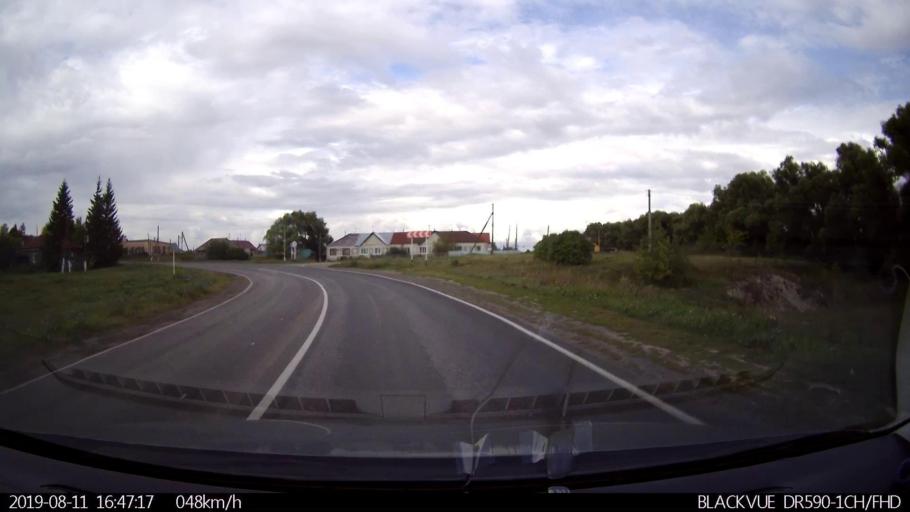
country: RU
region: Ulyanovsk
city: Mayna
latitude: 54.2018
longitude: 47.6956
